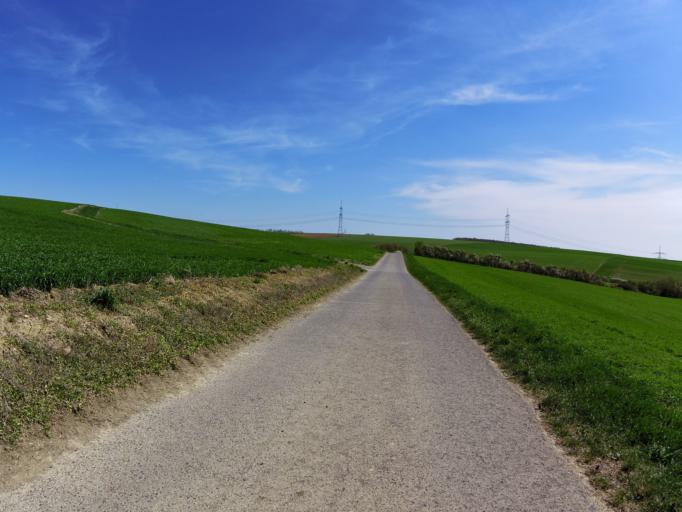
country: DE
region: Bavaria
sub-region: Regierungsbezirk Unterfranken
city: Rottendorf
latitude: 49.7921
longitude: 10.0426
